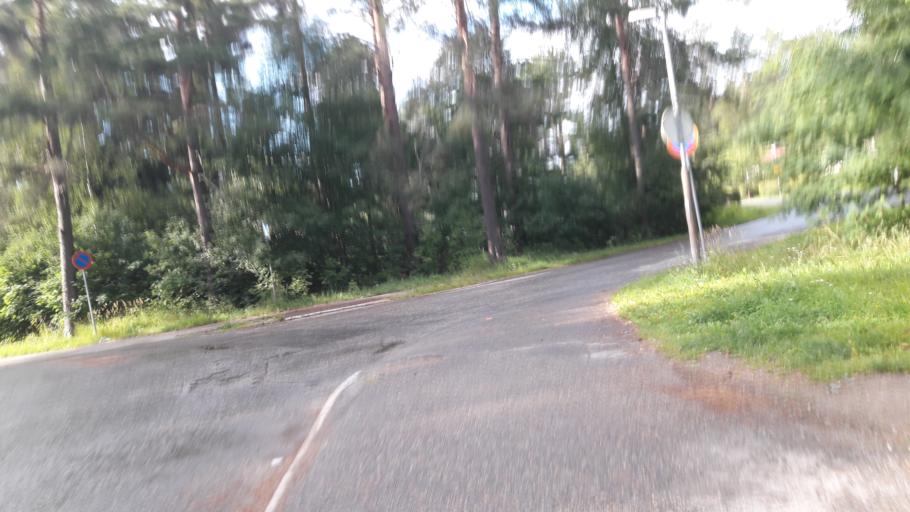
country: FI
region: North Karelia
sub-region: Joensuu
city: Joensuu
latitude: 62.5835
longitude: 29.7858
